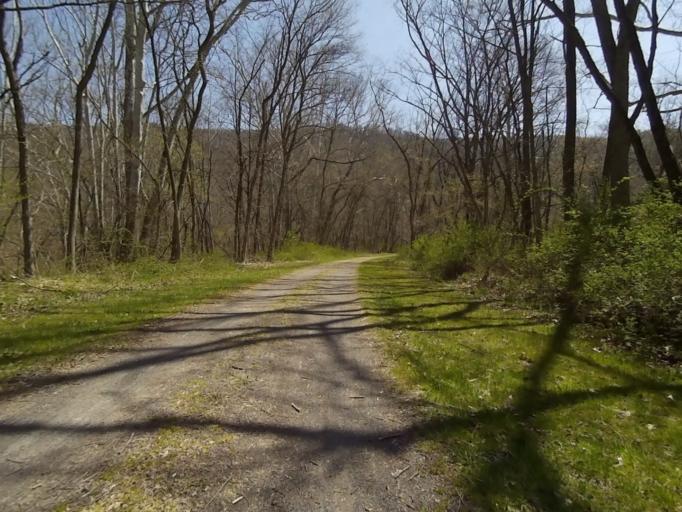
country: US
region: Pennsylvania
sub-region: Blair County
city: Williamsburg
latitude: 40.5083
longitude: -78.1665
